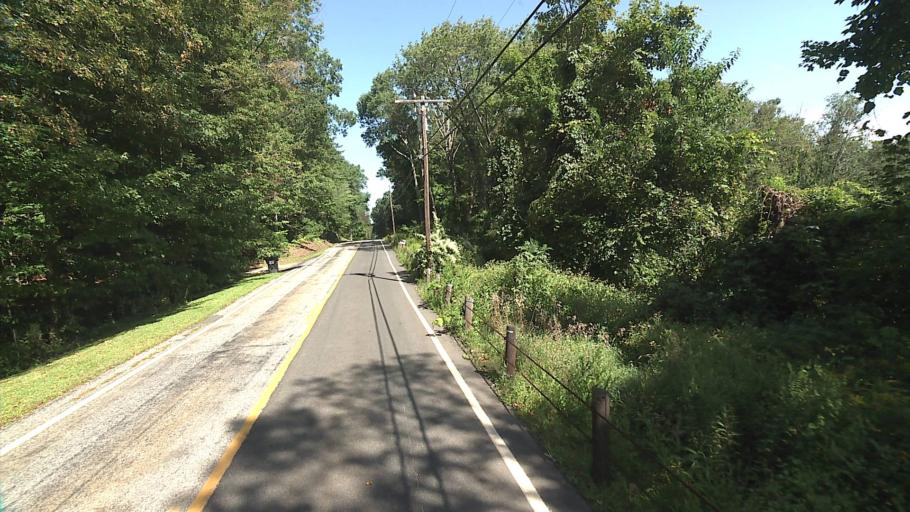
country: US
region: Connecticut
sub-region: Litchfield County
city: Northwest Harwinton
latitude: 41.7305
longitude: -73.0743
